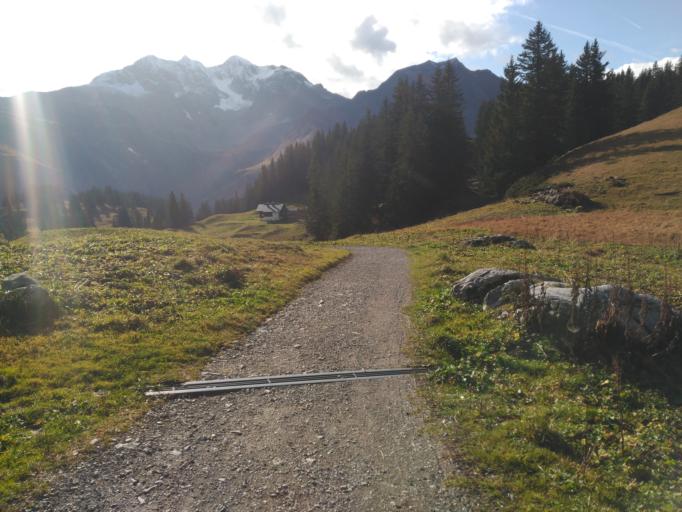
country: AT
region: Vorarlberg
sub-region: Politischer Bezirk Bregenz
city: Schroecken
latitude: 47.2583
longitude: 10.1117
